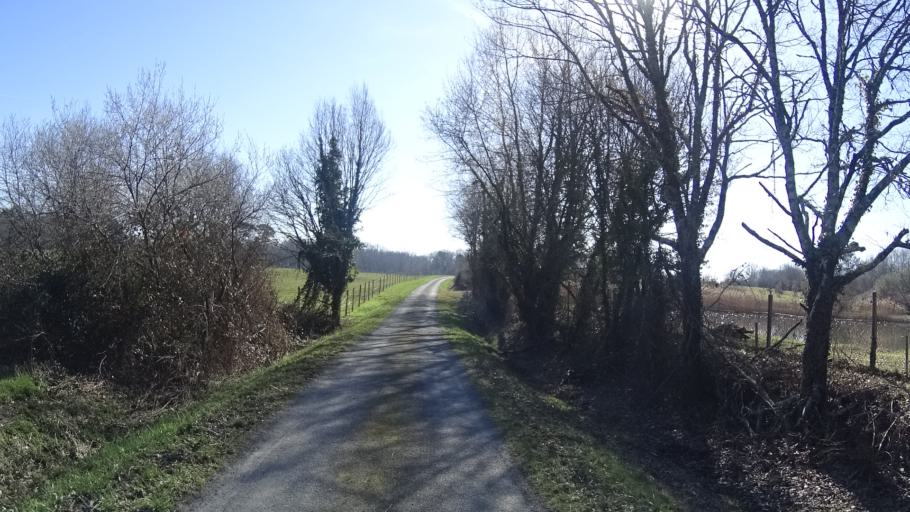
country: FR
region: Aquitaine
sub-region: Departement de la Dordogne
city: Saint-Aulaye
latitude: 45.1324
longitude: 0.2223
